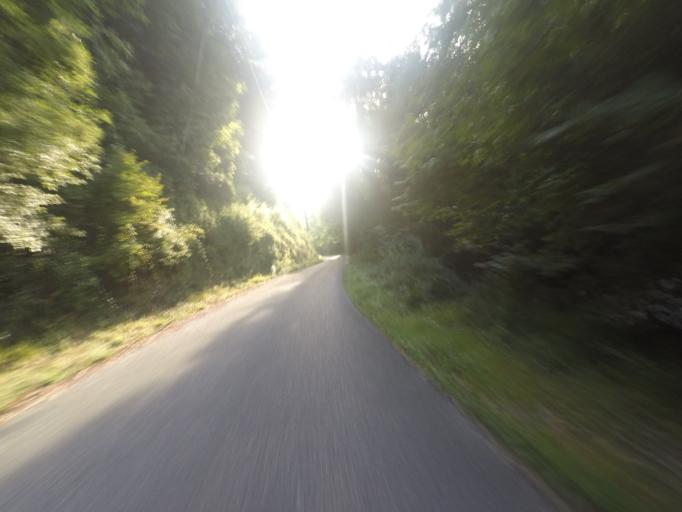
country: IT
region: Tuscany
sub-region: Provincia di Lucca
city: Pescaglia
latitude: 43.9435
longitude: 10.3960
